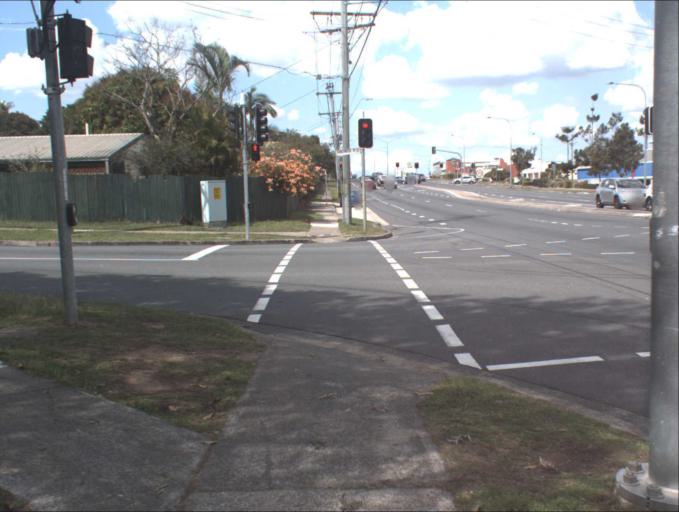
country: AU
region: Queensland
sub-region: Brisbane
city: Sunnybank Hills
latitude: -27.6615
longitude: 153.0457
